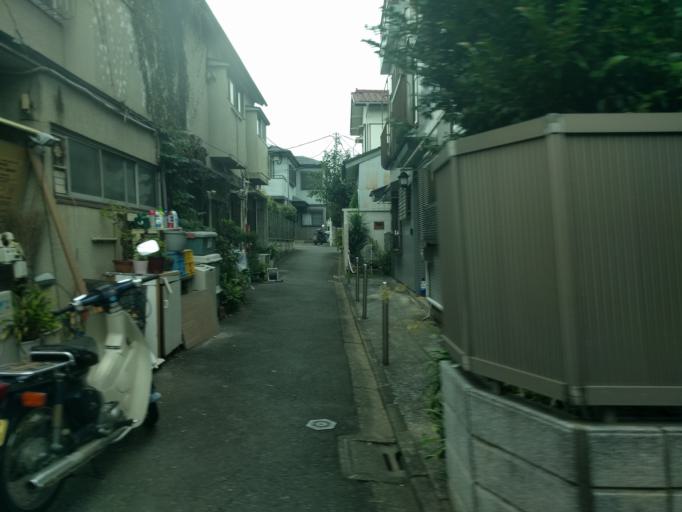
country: JP
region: Tokyo
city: Tokyo
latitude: 35.6354
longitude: 139.6979
